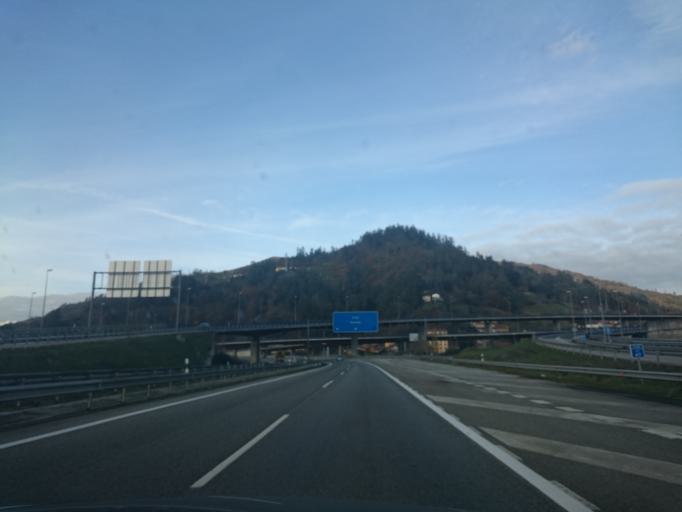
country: ES
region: Asturias
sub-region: Province of Asturias
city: Mieres
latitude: 43.2597
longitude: -5.7827
